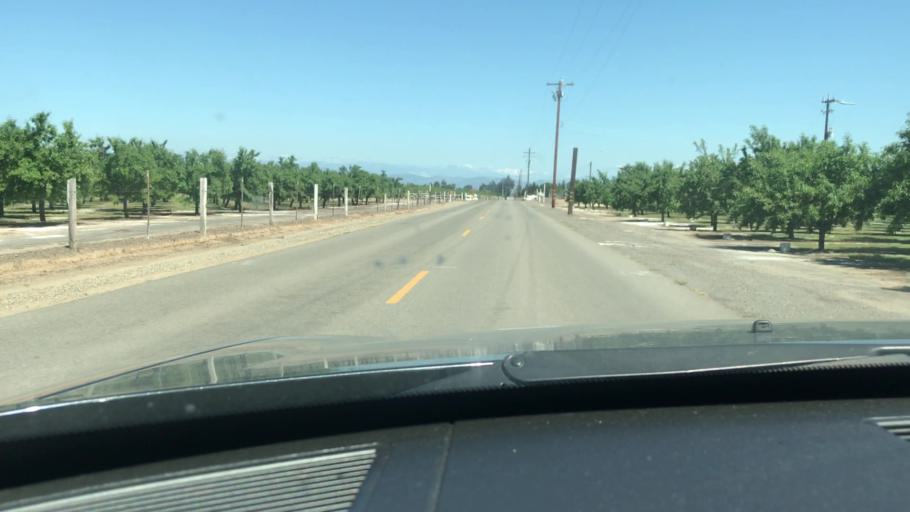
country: US
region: California
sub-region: Fresno County
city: Clovis
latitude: 36.8811
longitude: -119.7073
